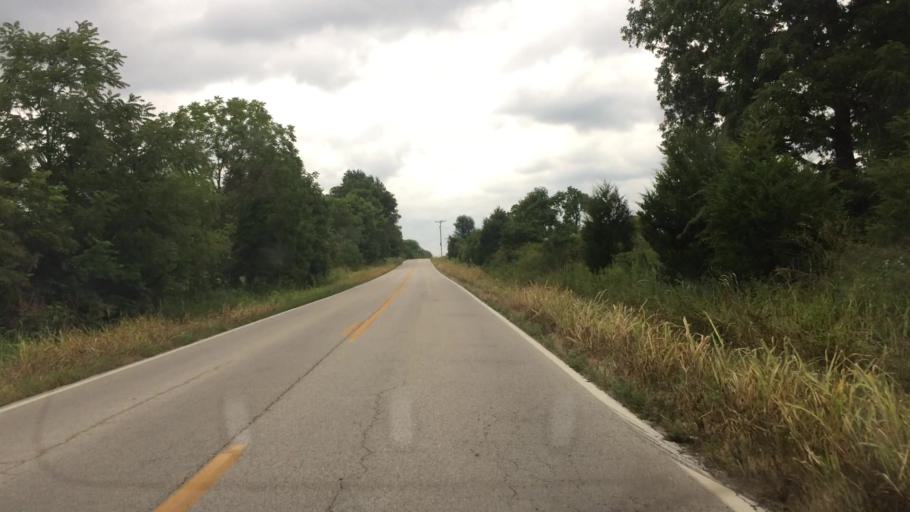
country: US
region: Missouri
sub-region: Greene County
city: Strafford
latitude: 37.2840
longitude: -93.1057
